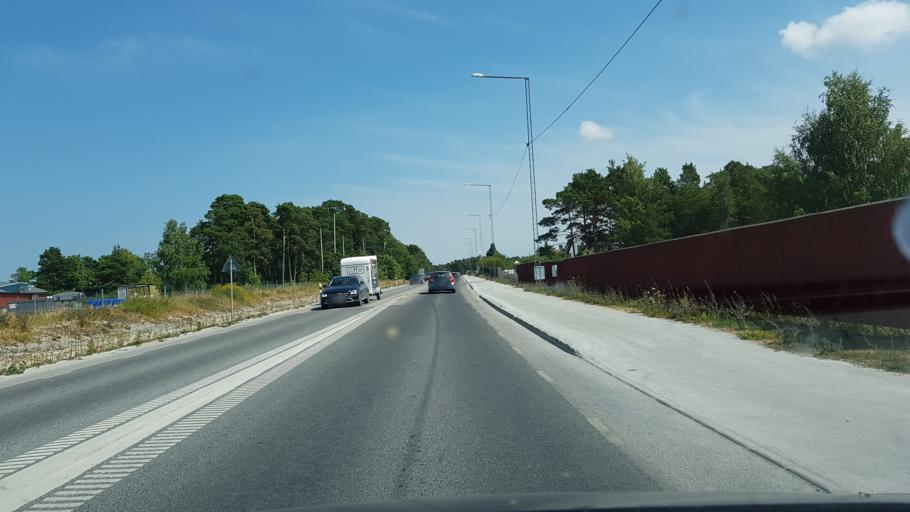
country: SE
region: Gotland
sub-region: Gotland
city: Visby
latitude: 57.6313
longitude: 18.3363
